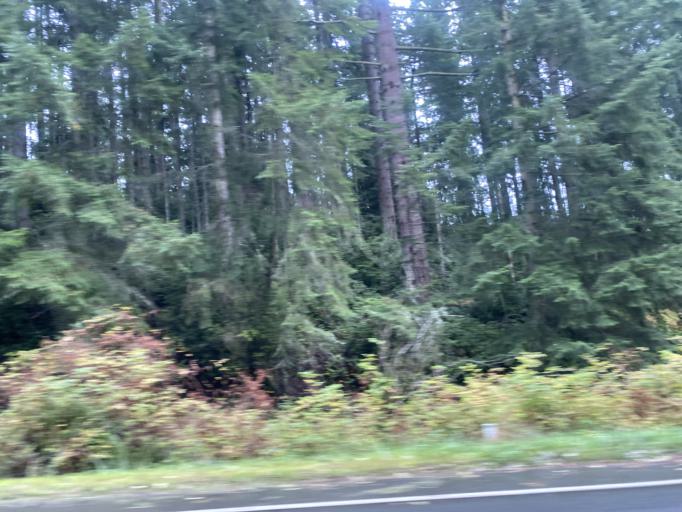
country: US
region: Washington
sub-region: Island County
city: Langley
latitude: 48.0487
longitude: -122.4454
